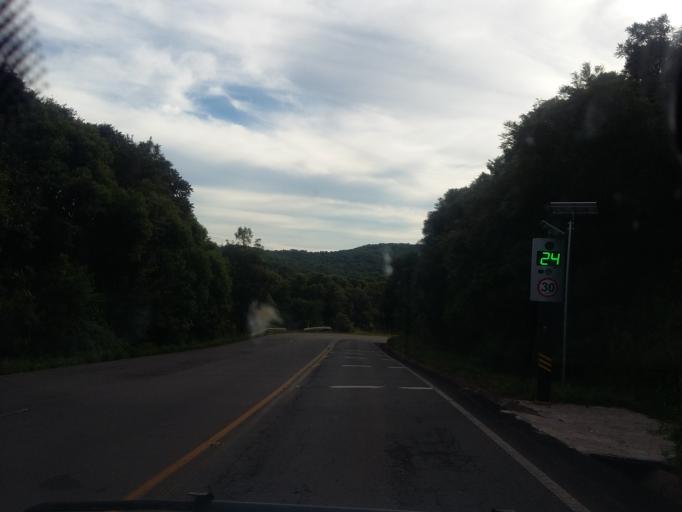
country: BR
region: Santa Catarina
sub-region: Celso Ramos
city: Celso Ramos
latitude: -27.6193
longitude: -51.4861
